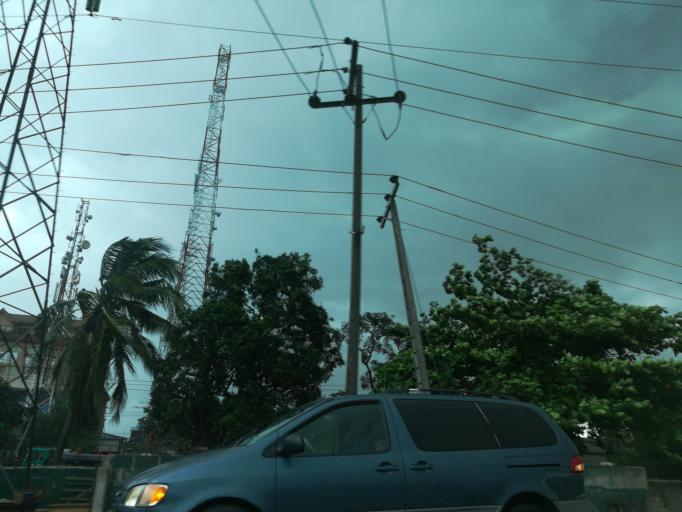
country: NG
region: Lagos
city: Ojota
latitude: 6.5955
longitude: 3.3848
